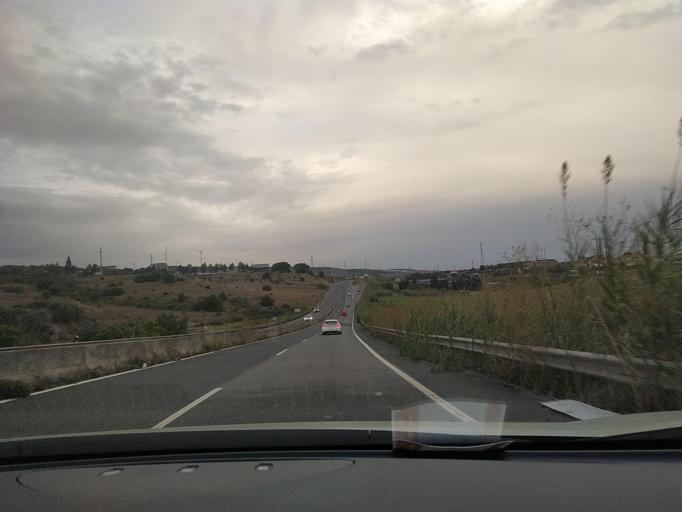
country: PT
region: Lisbon
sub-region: Loures
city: Santo Antao do Tojal
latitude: 38.8610
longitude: -9.1416
